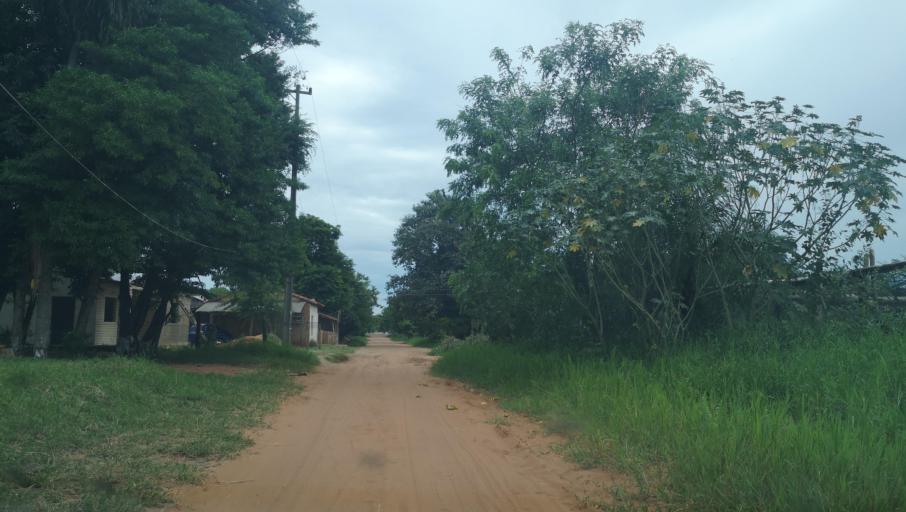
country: PY
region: San Pedro
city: Capiibary
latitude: -24.7402
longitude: -56.0221
